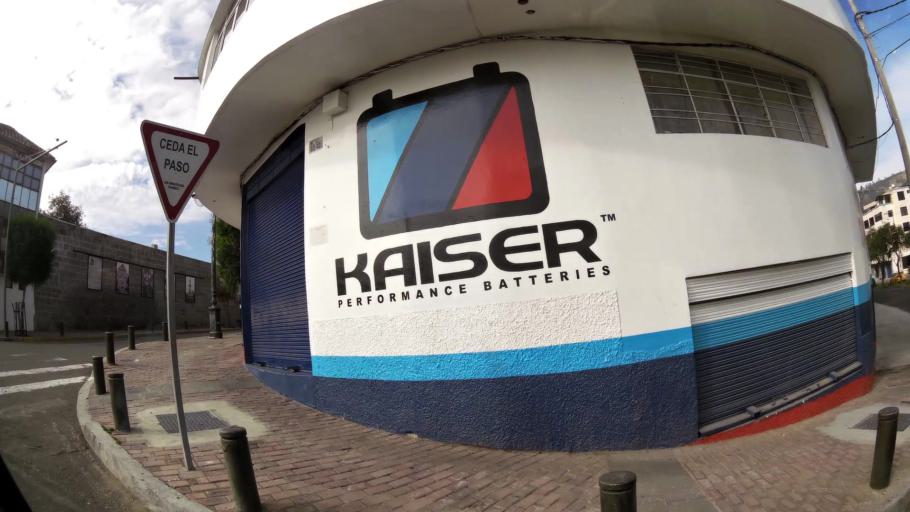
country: EC
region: Tungurahua
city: Ambato
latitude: -1.2295
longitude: -78.6199
